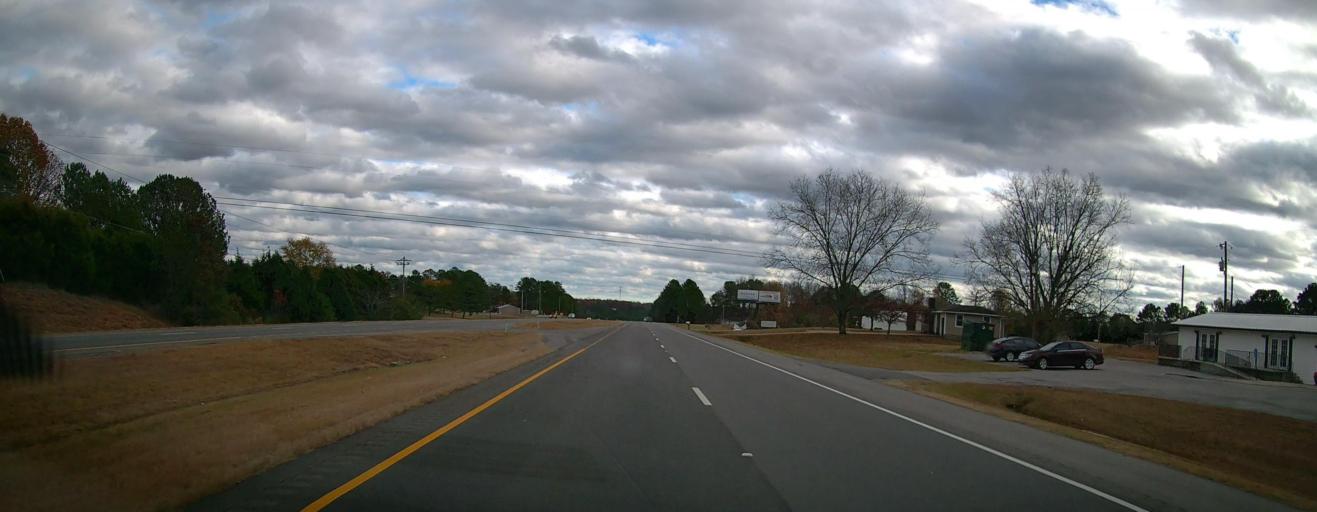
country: US
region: Alabama
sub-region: Cullman County
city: Cullman
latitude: 34.2176
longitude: -86.8950
